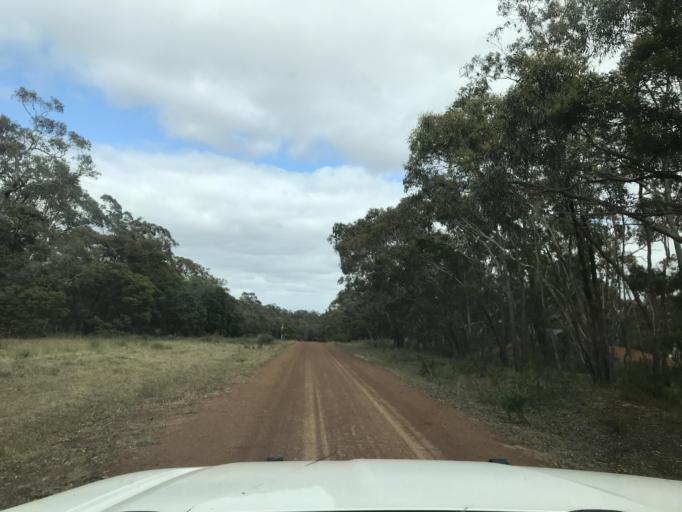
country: AU
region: South Australia
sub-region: Wattle Range
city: Penola
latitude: -37.3344
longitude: 141.4146
